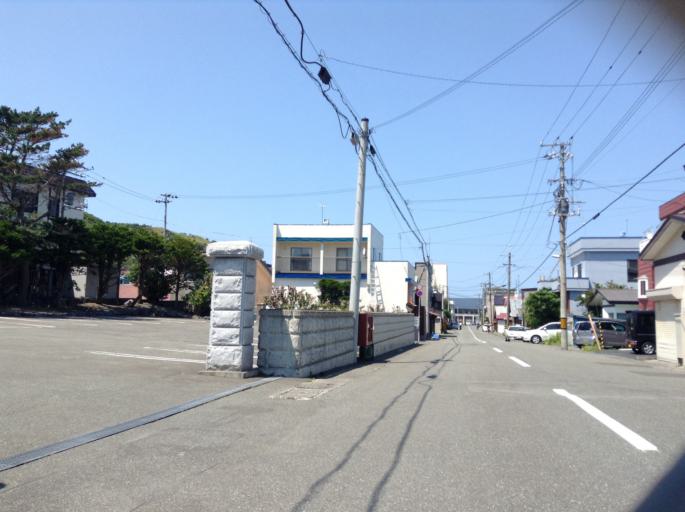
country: JP
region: Hokkaido
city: Wakkanai
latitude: 45.4238
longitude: 141.6709
